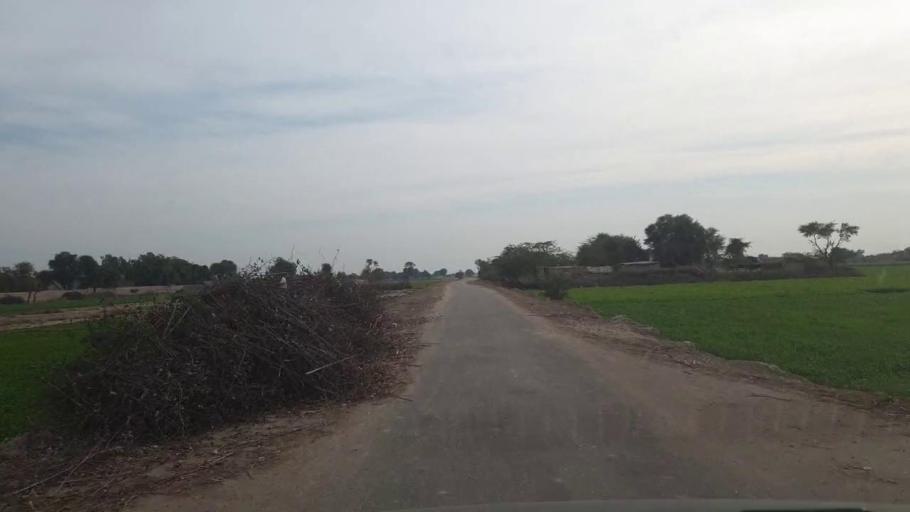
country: PK
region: Sindh
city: Shahpur Chakar
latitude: 26.1053
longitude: 68.5232
